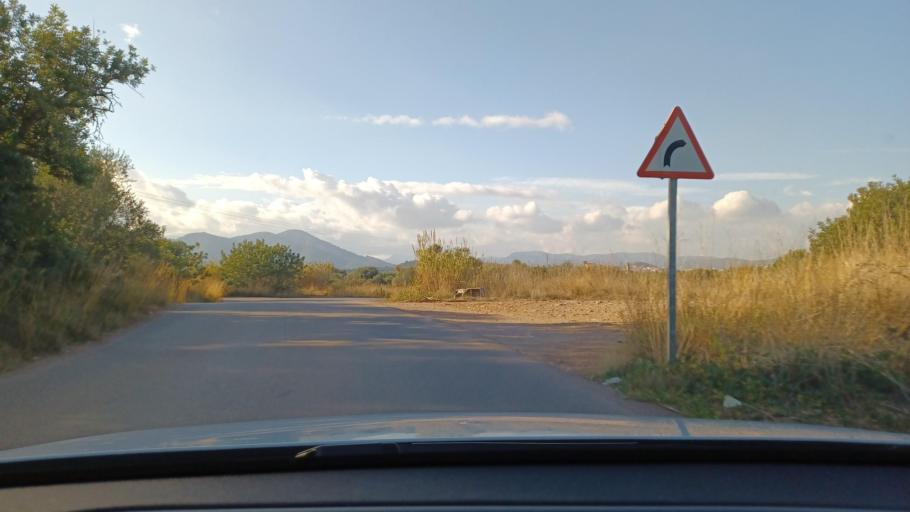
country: ES
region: Valencia
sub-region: Provincia de Castello
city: Betxi
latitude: 39.9466
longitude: -0.2221
